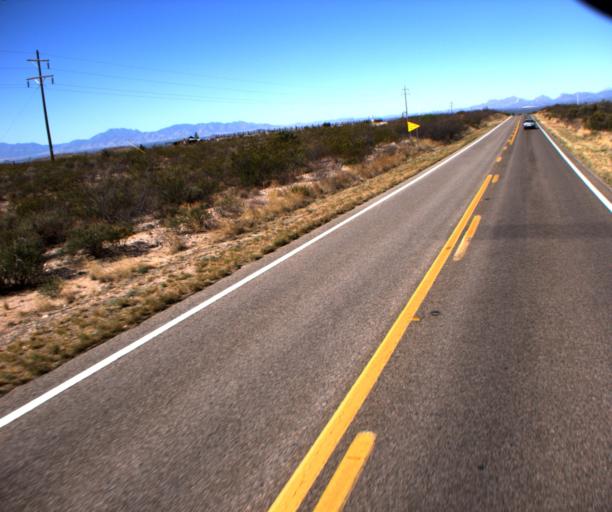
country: US
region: Arizona
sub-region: Cochise County
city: Tombstone
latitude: 31.7471
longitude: -110.1178
